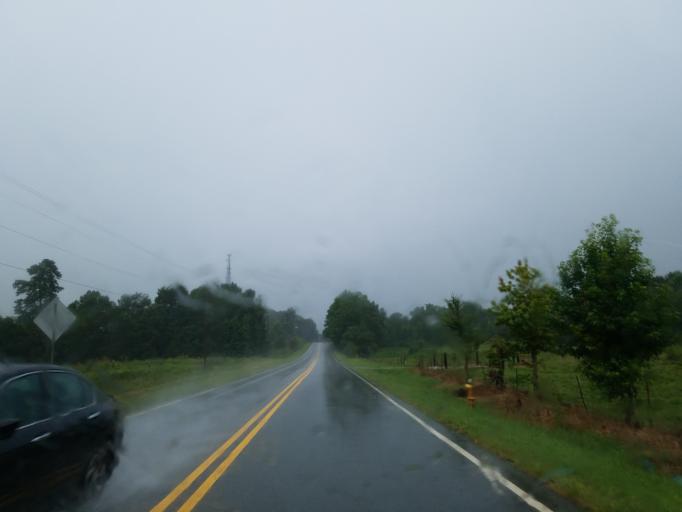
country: US
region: Georgia
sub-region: Floyd County
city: Shannon
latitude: 34.3696
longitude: -85.0642
